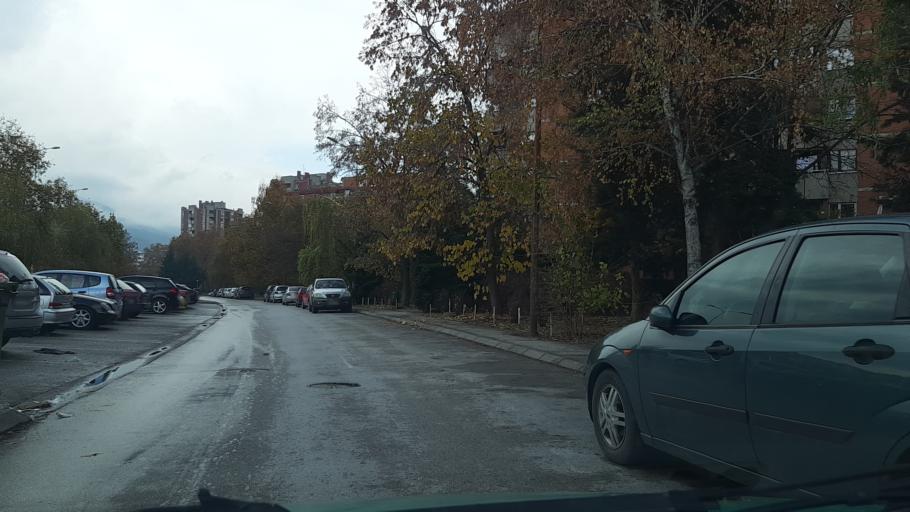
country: MK
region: Karpos
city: Skopje
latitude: 41.9895
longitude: 21.4580
